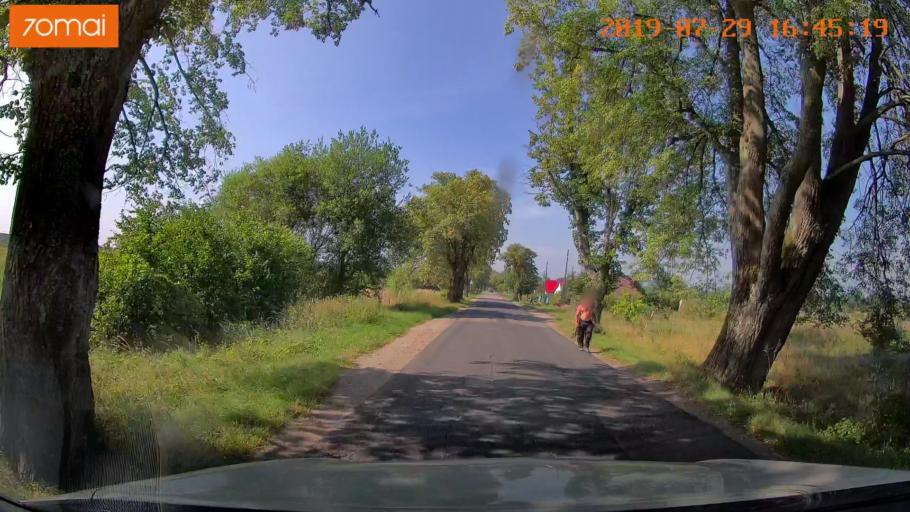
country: RU
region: Kaliningrad
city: Primorsk
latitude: 54.7638
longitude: 20.0812
